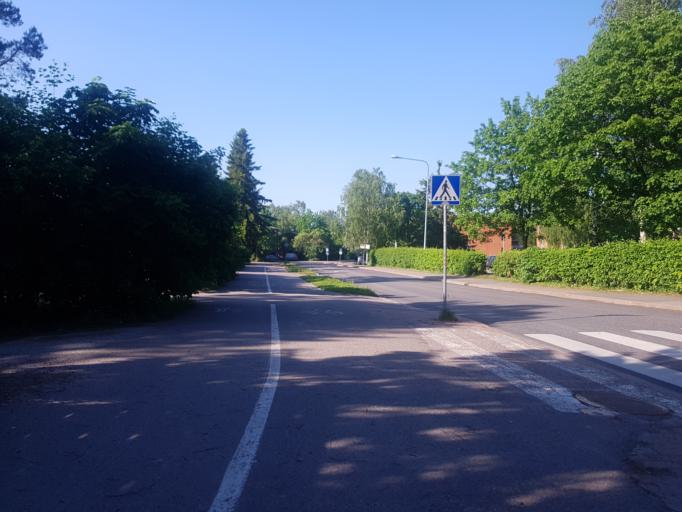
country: FI
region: Uusimaa
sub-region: Helsinki
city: Vantaa
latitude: 60.2533
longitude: 24.9937
